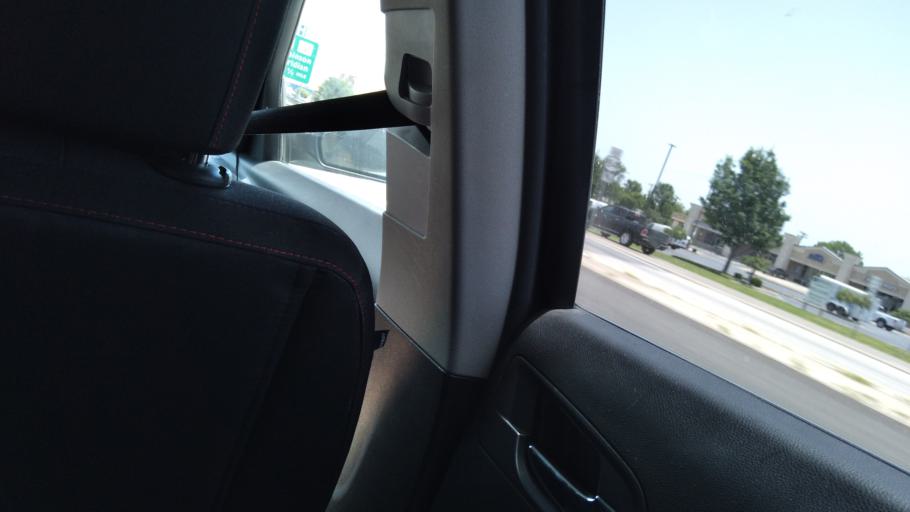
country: US
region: Texas
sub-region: McLennan County
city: Woodway
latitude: 31.5082
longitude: -97.1967
